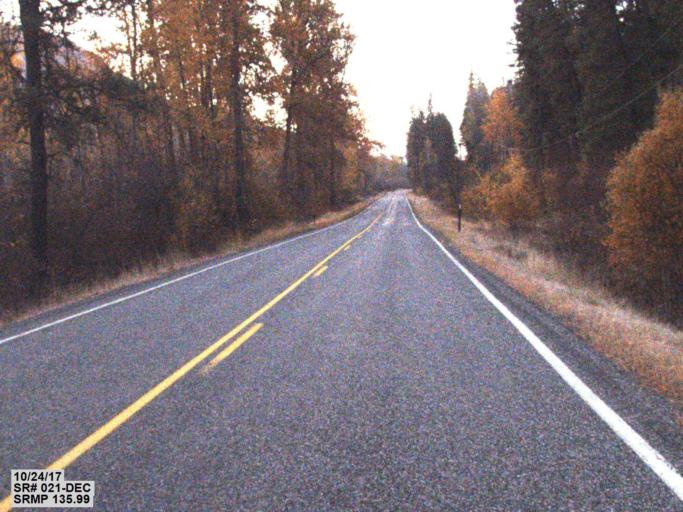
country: US
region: Washington
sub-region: Ferry County
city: Republic
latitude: 48.3343
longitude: -118.7481
